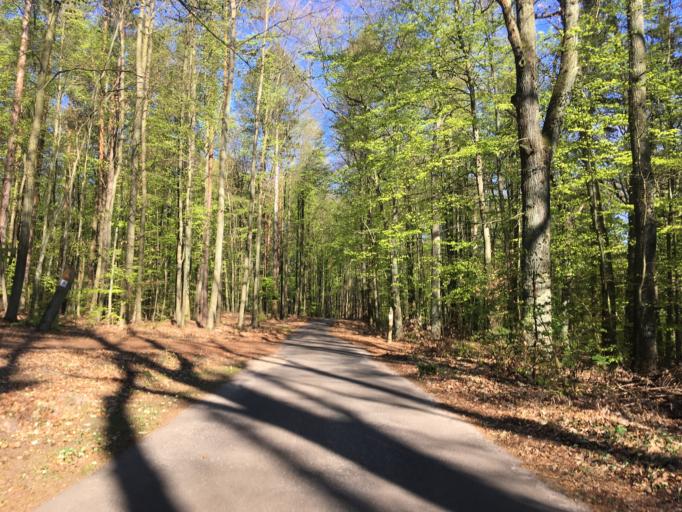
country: DE
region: Brandenburg
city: Wandlitz
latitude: 52.7391
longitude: 13.4960
